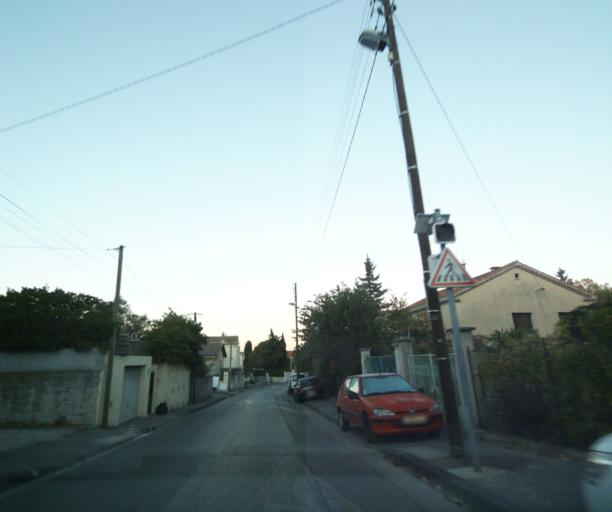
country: FR
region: Provence-Alpes-Cote d'Azur
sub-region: Departement des Bouches-du-Rhone
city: La Penne-sur-Huveaune
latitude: 43.3003
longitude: 5.5127
